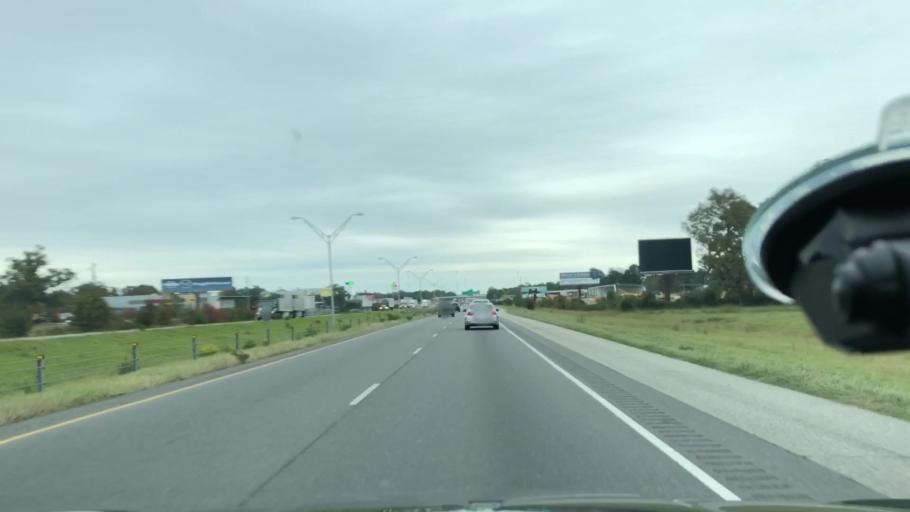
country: US
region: Arkansas
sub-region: Miller County
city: Texarkana
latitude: 33.4734
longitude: -94.0179
